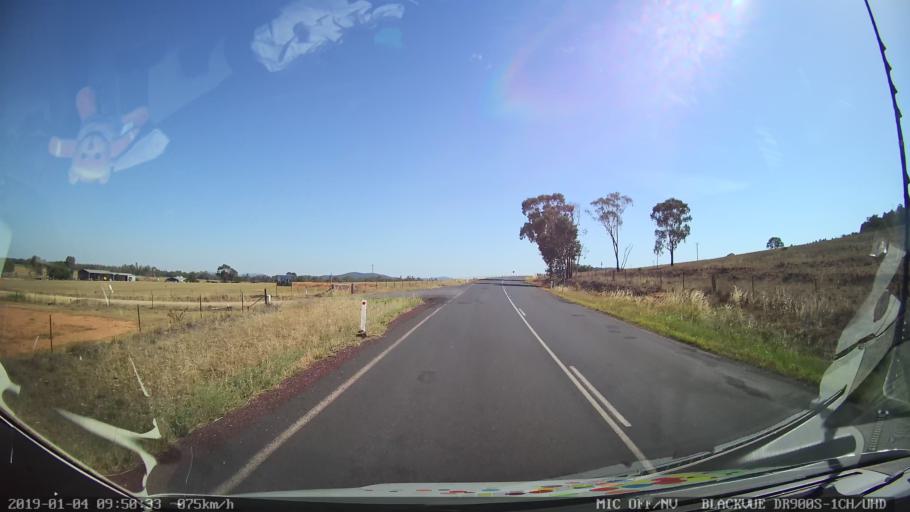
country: AU
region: New South Wales
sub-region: Cabonne
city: Canowindra
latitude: -33.5829
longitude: 148.4158
